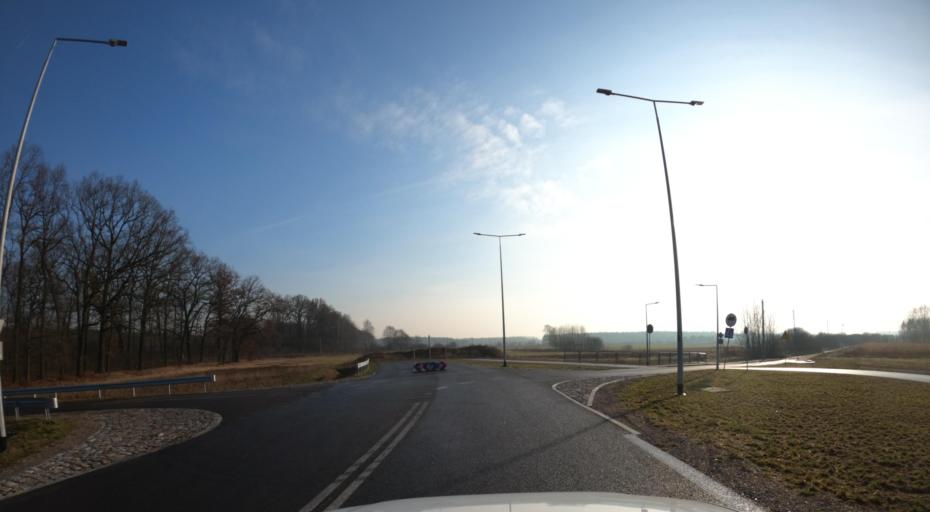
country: PL
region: Lubusz
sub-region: Powiat gorzowski
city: Kostrzyn nad Odra
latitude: 52.6228
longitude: 14.6257
